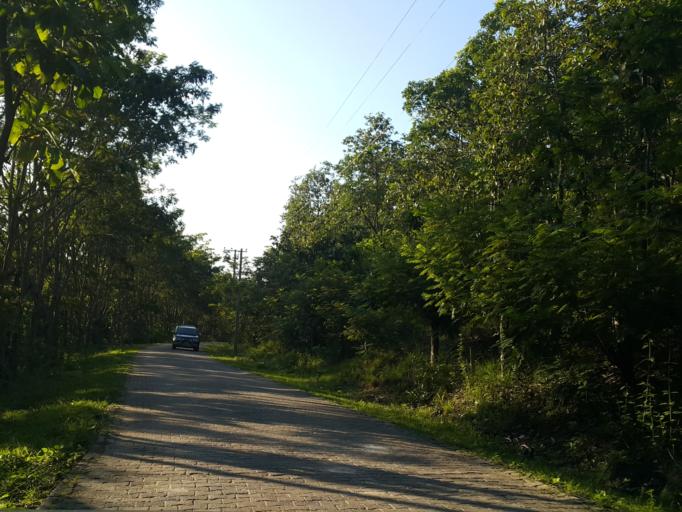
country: TH
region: Chiang Mai
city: Mae On
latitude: 18.7079
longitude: 99.2062
